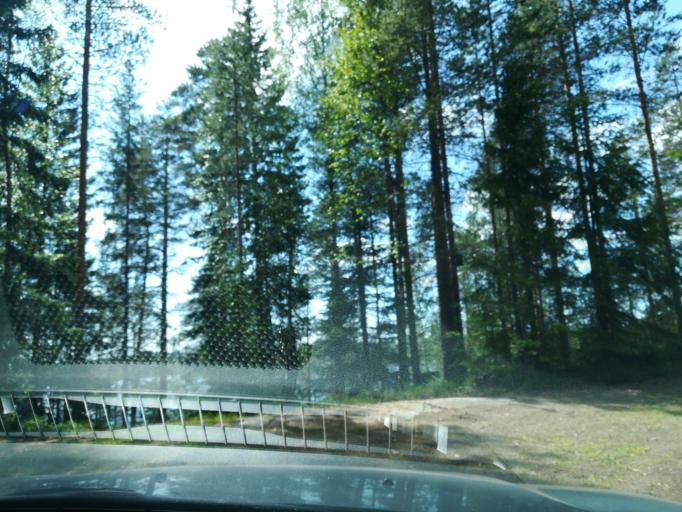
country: FI
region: South Karelia
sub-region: Imatra
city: Ruokolahti
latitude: 61.4817
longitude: 28.8701
